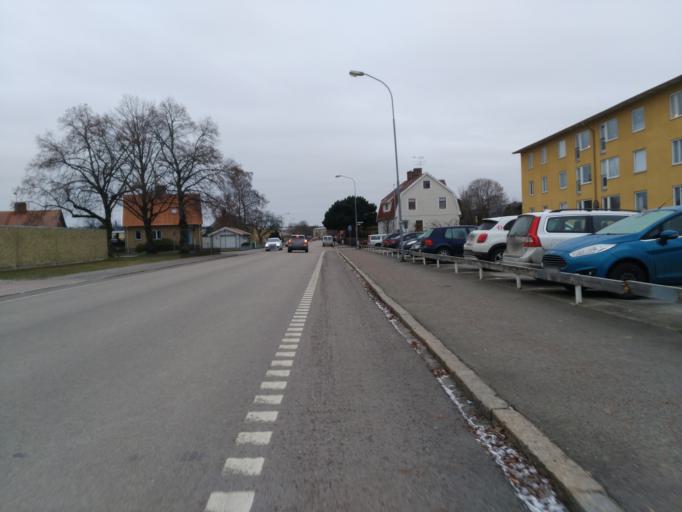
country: SE
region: Vaestra Goetaland
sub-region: Lidkopings Kommun
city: Lidkoping
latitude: 58.4965
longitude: 13.1595
